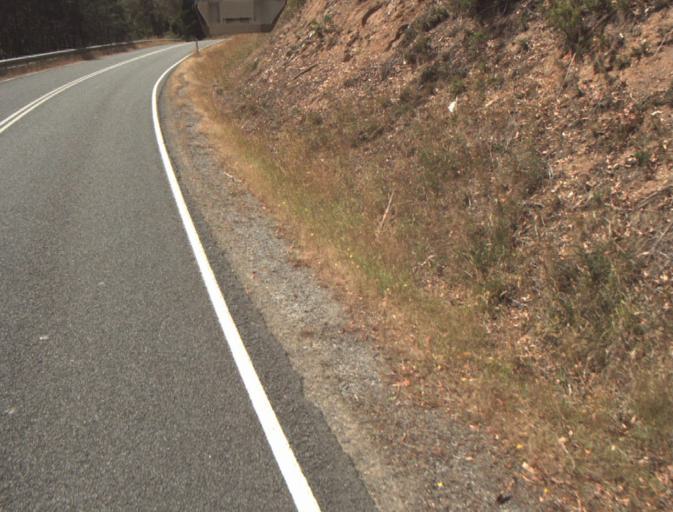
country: AU
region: Tasmania
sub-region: Dorset
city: Scottsdale
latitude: -41.3000
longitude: 147.3827
